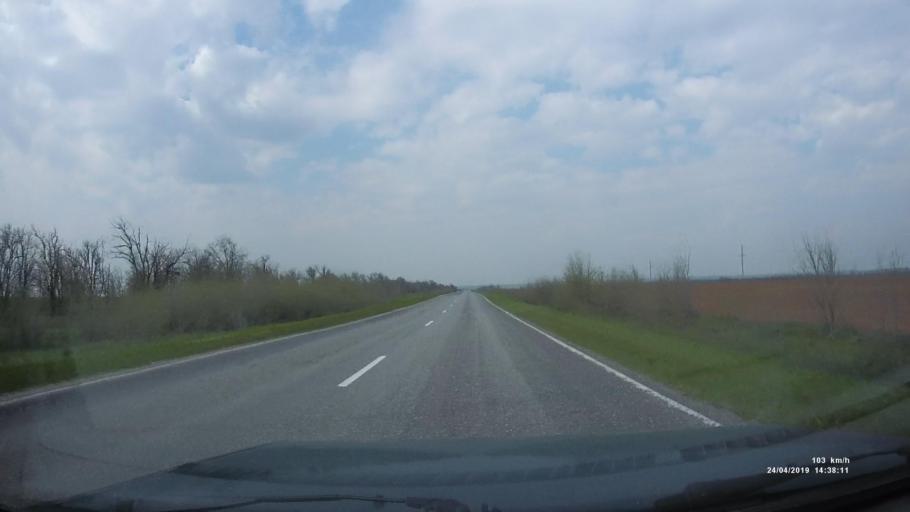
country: RU
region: Rostov
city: Remontnoye
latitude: 46.3977
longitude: 43.8861
